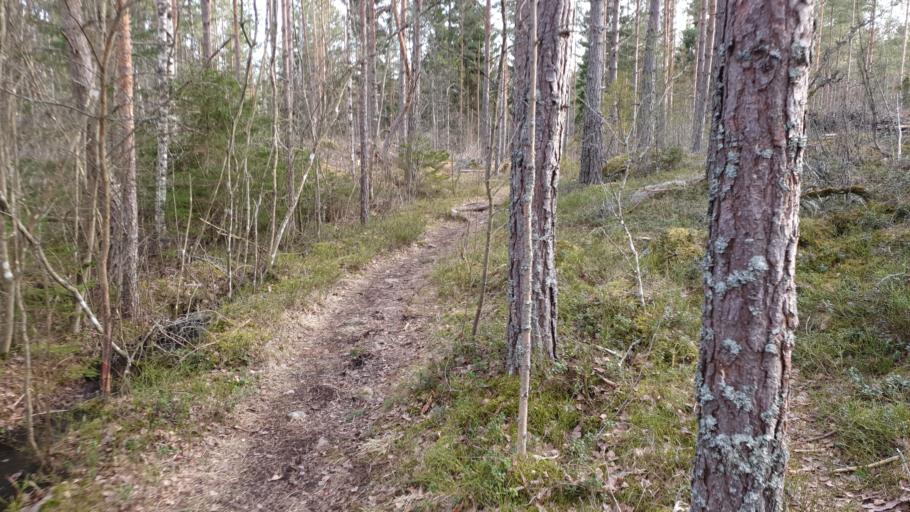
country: SE
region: Uppsala
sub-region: Enkopings Kommun
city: Grillby
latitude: 59.6006
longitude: 17.1647
